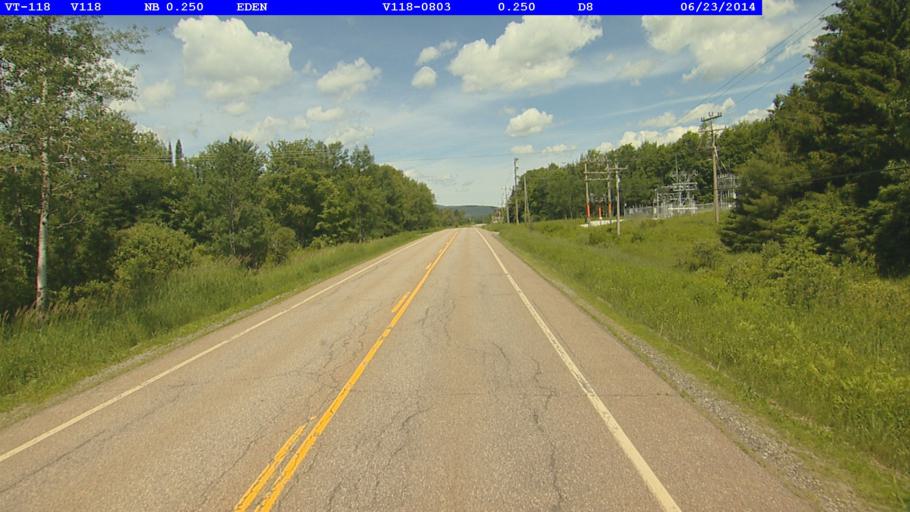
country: US
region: Vermont
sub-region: Lamoille County
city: Hyde Park
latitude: 44.7102
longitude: -72.5487
